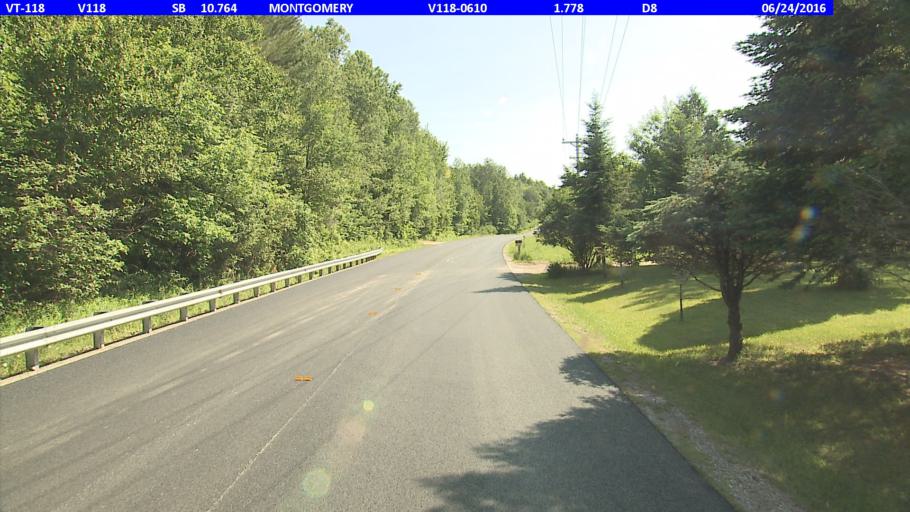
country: US
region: Vermont
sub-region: Franklin County
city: Richford
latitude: 44.8236
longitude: -72.6101
